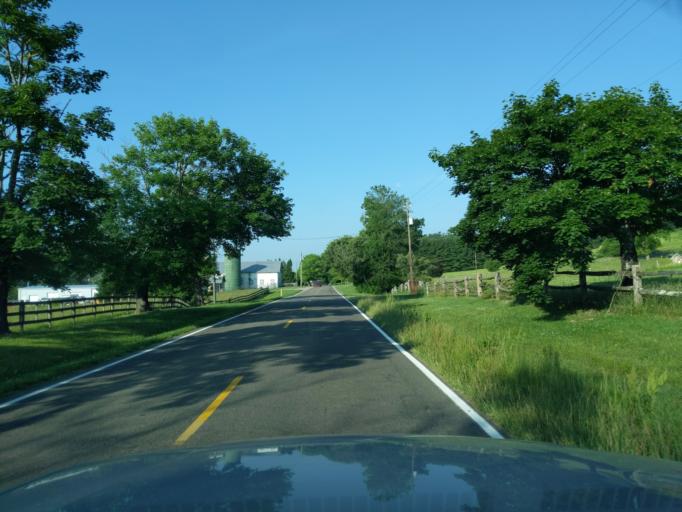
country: US
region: North Carolina
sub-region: Henderson County
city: Hoopers Creek
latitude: 35.4681
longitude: -82.4601
